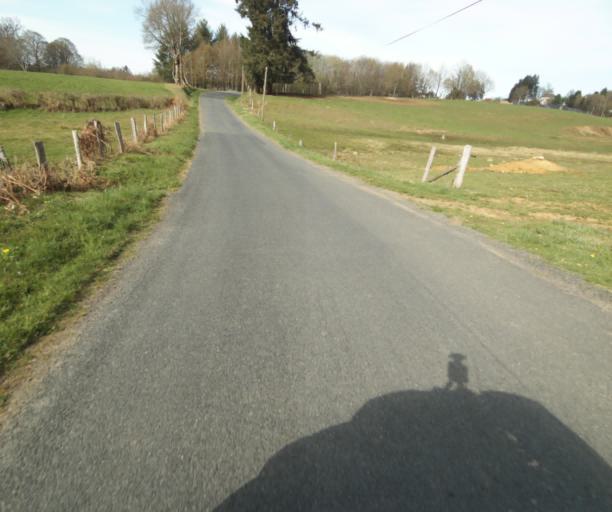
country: FR
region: Limousin
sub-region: Departement de la Correze
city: Naves
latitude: 45.3310
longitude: 1.7441
